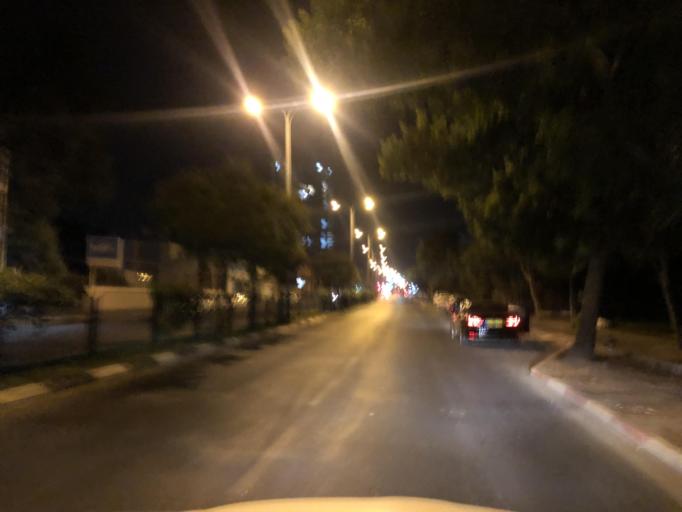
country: IL
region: Tel Aviv
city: Azor
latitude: 32.0473
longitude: 34.7966
